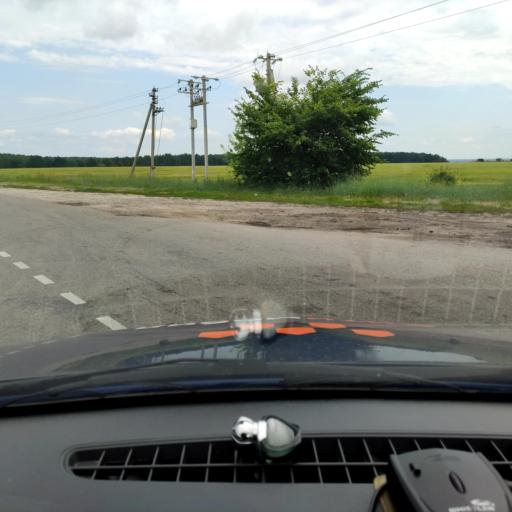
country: RU
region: Voronezj
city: Ramon'
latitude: 52.0157
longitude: 39.3347
